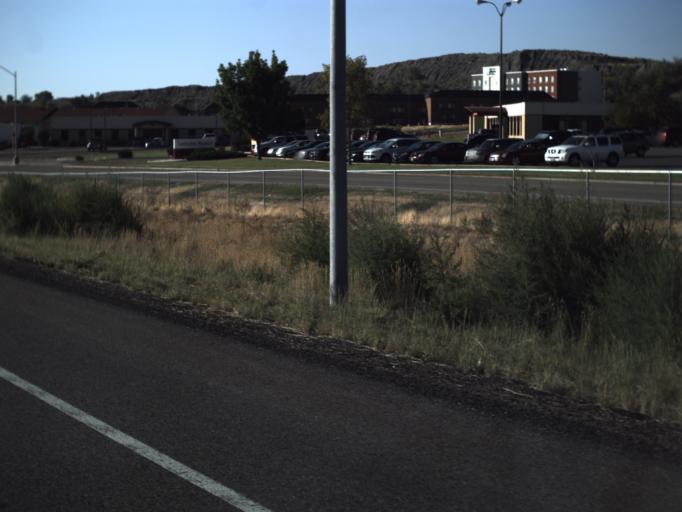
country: US
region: Utah
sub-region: Carbon County
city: Carbonville
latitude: 39.6056
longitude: -110.8316
